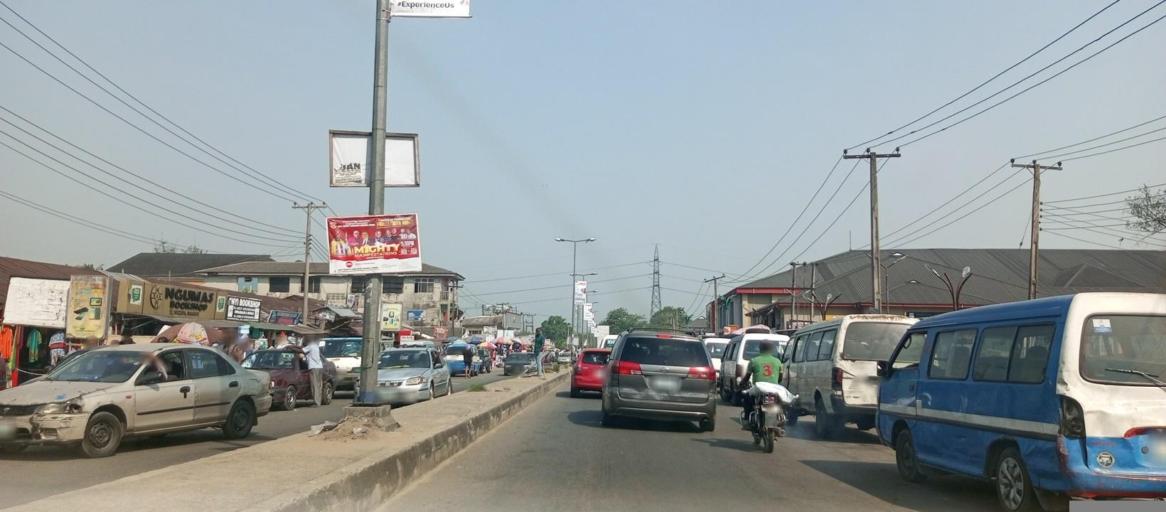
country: NG
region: Rivers
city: Emuoha
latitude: 4.8968
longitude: 6.9076
